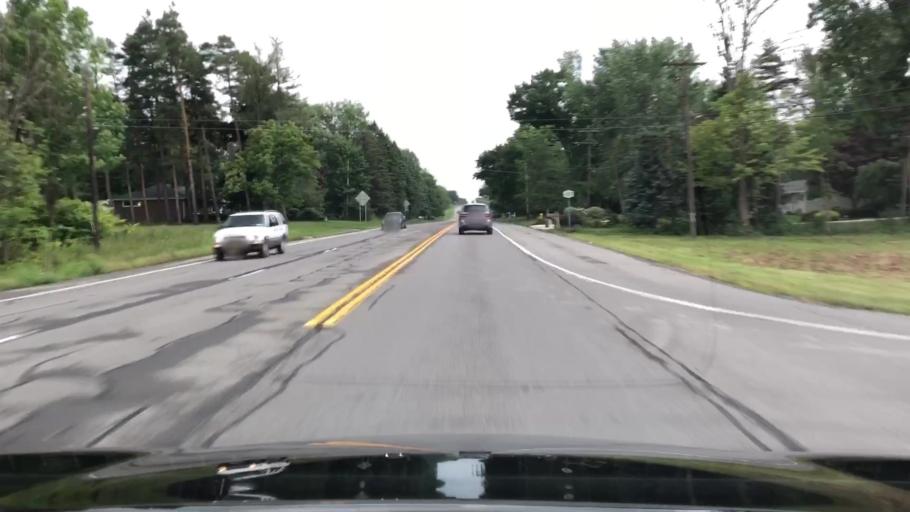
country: US
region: New York
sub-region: Erie County
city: Elma Center
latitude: 42.8112
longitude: -78.6969
